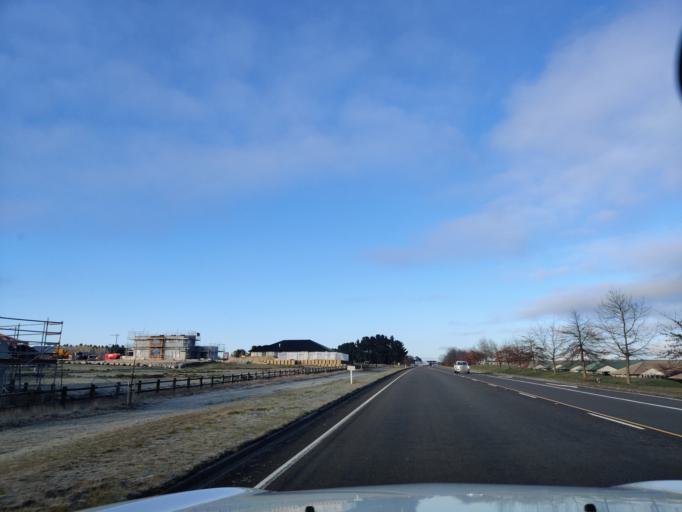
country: NZ
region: Waikato
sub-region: Taupo District
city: Taupo
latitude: -38.7288
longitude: 176.0745
